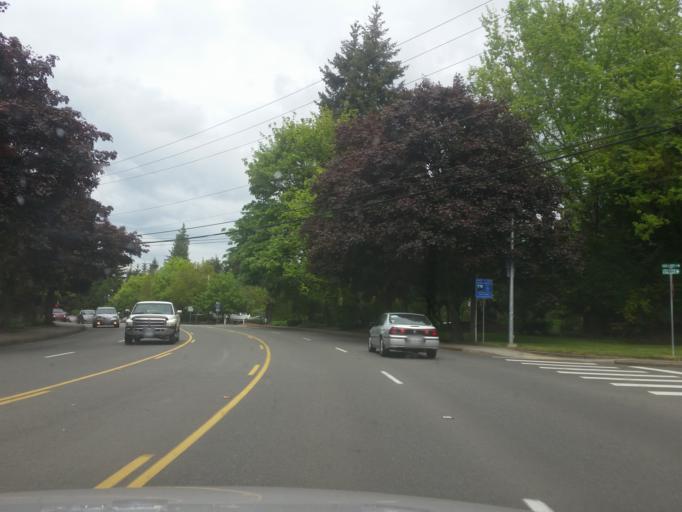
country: US
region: Washington
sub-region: King County
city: Inglewood-Finn Hill
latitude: 47.7096
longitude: -122.2081
